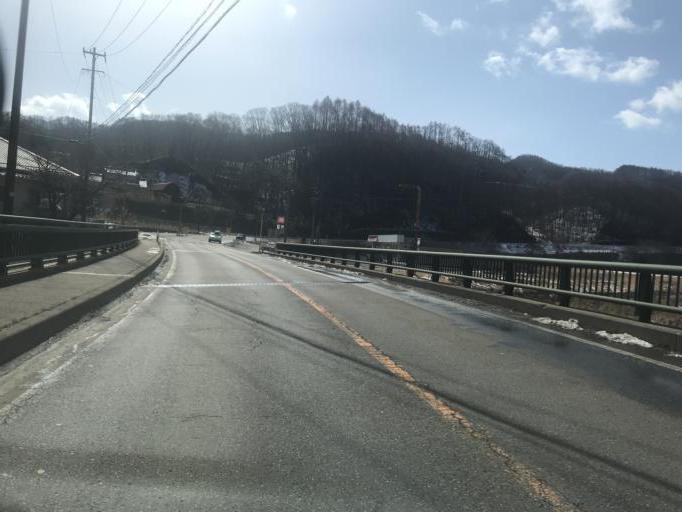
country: JP
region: Nagano
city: Saku
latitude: 36.0091
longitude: 138.4941
